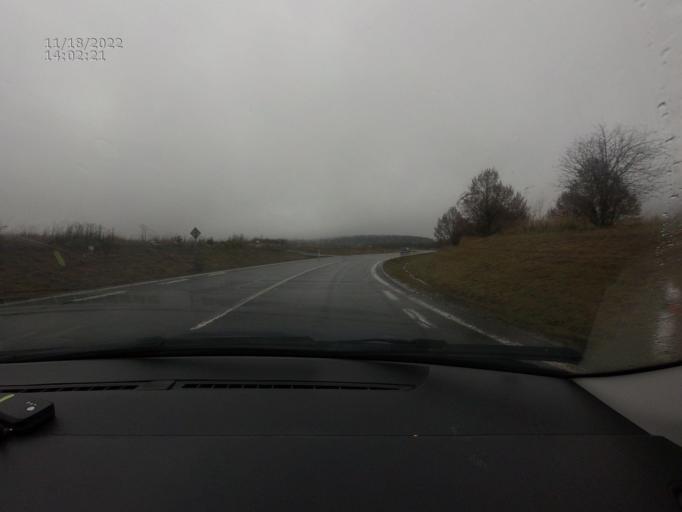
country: CZ
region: Jihocesky
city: Mirotice
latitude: 49.3500
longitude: 14.0499
